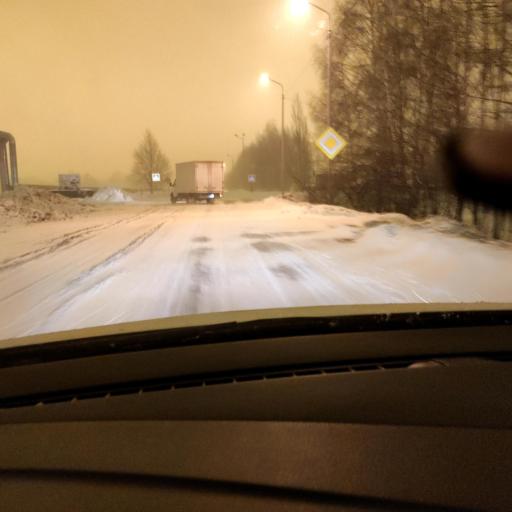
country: RU
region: Tatarstan
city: Osinovo
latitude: 55.8740
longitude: 48.9011
